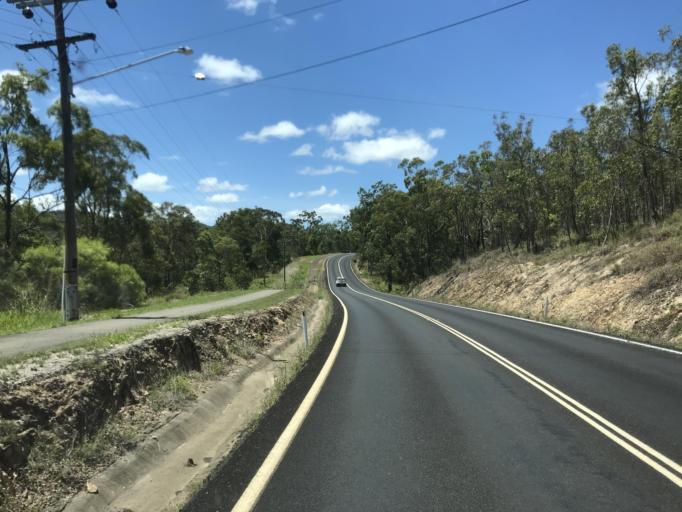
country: AU
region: Queensland
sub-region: Tablelands
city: Atherton
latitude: -17.3950
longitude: 145.3884
